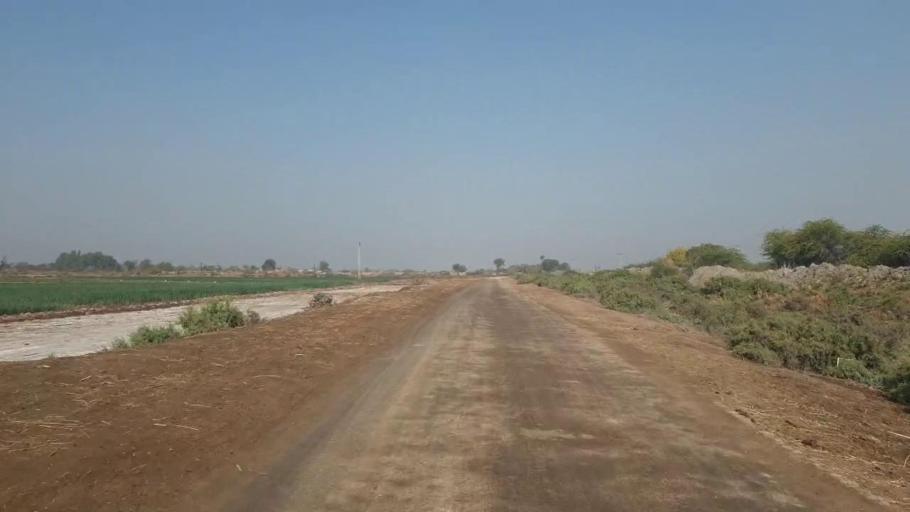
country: PK
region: Sindh
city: Mirwah Gorchani
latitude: 25.3719
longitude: 69.1877
